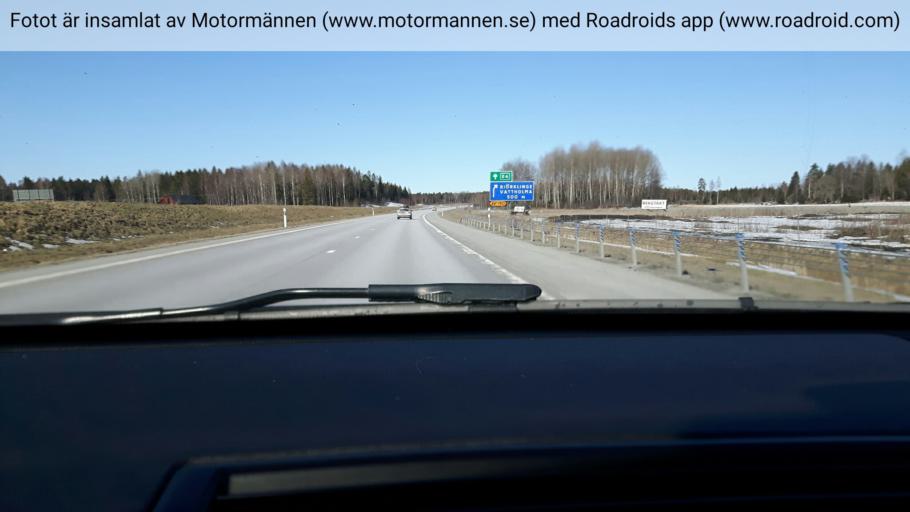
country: SE
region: Uppsala
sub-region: Uppsala Kommun
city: Storvreta
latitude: 60.0031
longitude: 17.6305
